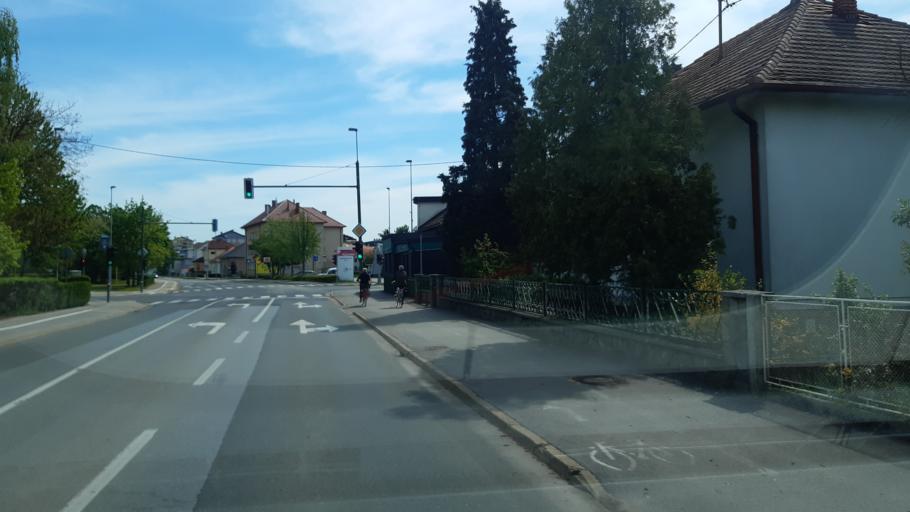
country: SI
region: Murska Sobota
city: Murska Sobota
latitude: 46.6611
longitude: 16.1535
